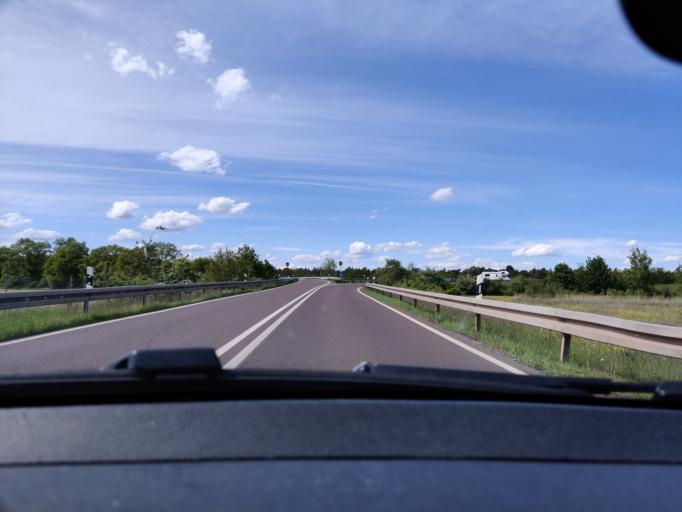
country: DE
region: Saxony-Anhalt
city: Burg bei Magdeburg
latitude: 52.2311
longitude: 11.8912
